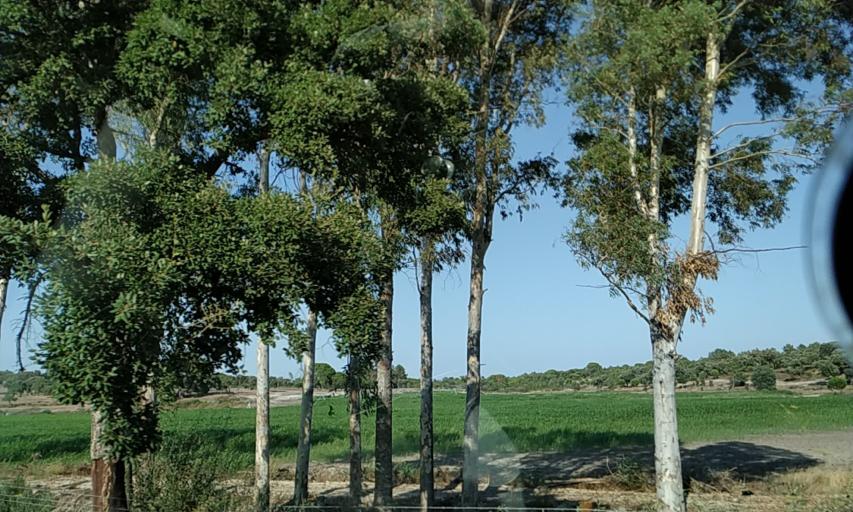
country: PT
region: Santarem
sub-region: Coruche
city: Coruche
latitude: 38.9949
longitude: -8.5552
